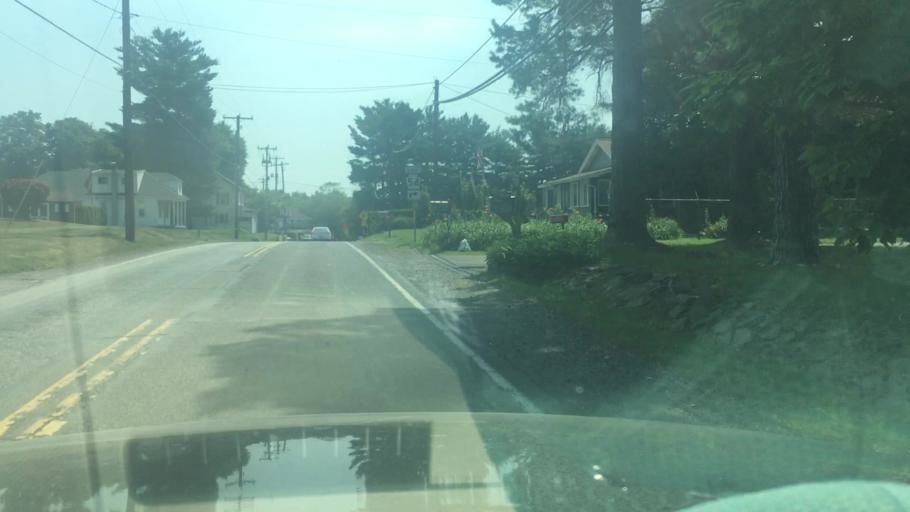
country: US
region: Pennsylvania
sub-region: Schuylkill County
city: Hometown
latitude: 40.8172
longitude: -76.0497
